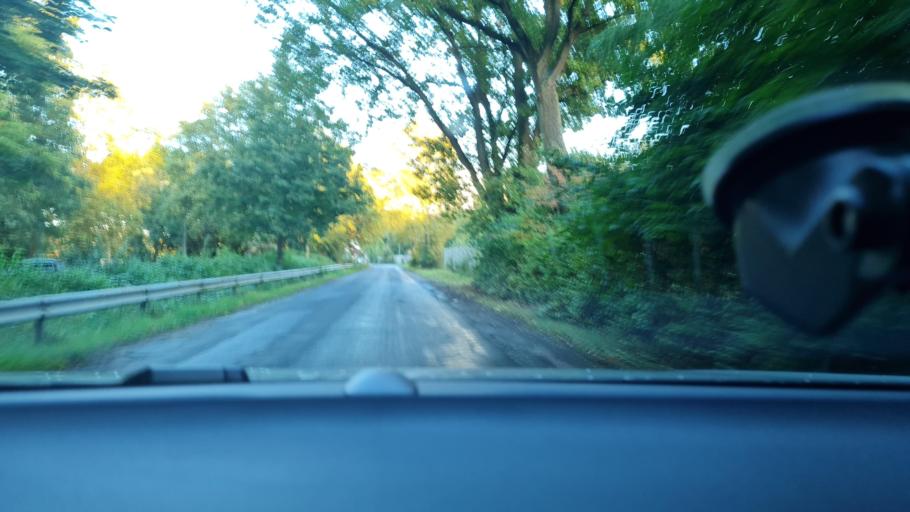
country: DE
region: North Rhine-Westphalia
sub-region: Regierungsbezirk Dusseldorf
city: Dinslaken
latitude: 51.5925
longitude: 6.7235
